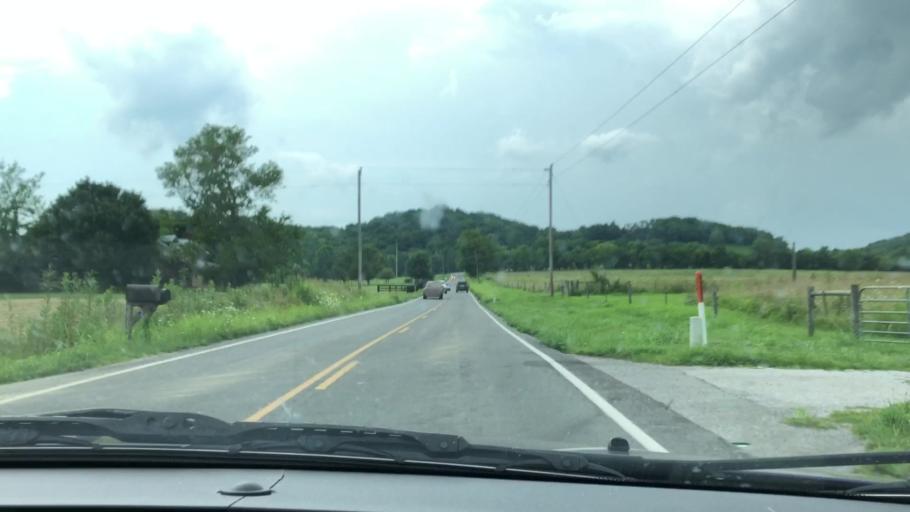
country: US
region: Tennessee
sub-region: Maury County
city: Spring Hill
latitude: 35.7885
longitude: -87.0038
